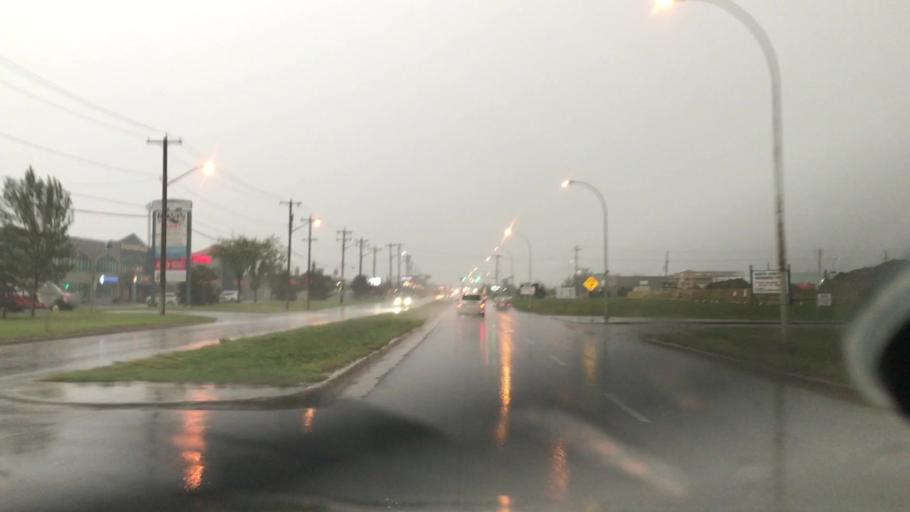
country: CA
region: Alberta
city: Edmonton
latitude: 53.5030
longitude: -113.4426
